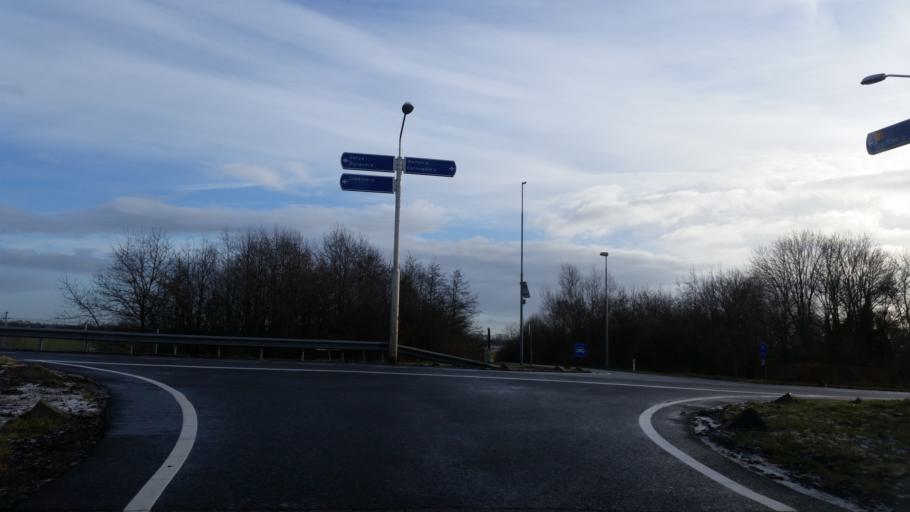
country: NL
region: Friesland
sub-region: Gemeente Tytsjerksteradiel
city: Garyp
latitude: 53.1602
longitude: 5.9519
